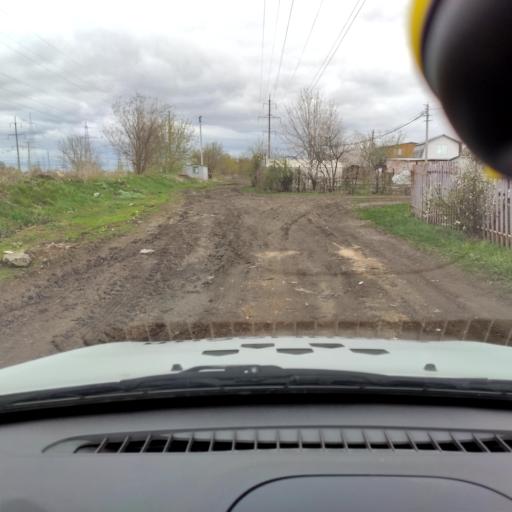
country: RU
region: Samara
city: Tol'yatti
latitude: 53.5866
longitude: 49.3202
